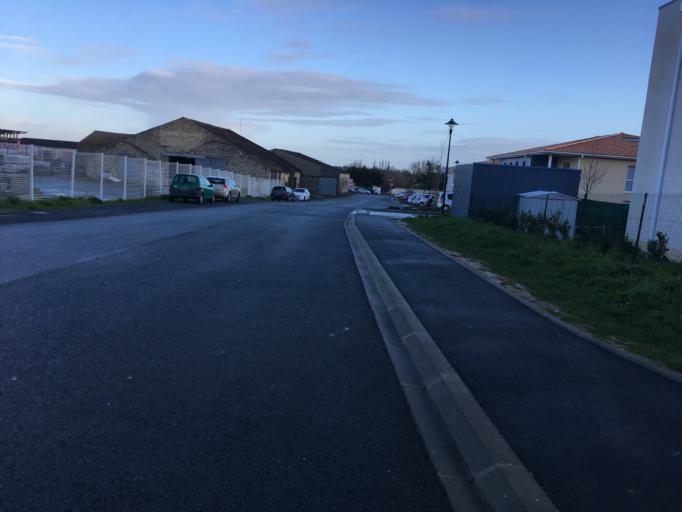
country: FR
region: Poitou-Charentes
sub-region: Departement de la Charente-Maritime
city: Nieul-sur-Mer
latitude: 46.2019
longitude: -1.1661
